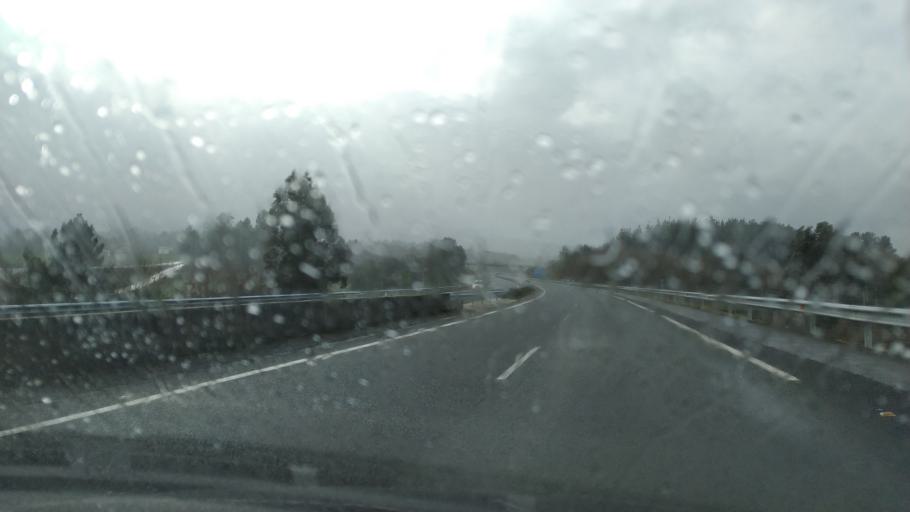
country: ES
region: Galicia
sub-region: Provincia de Pontevedra
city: Silleda
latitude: 42.7200
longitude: -8.2816
